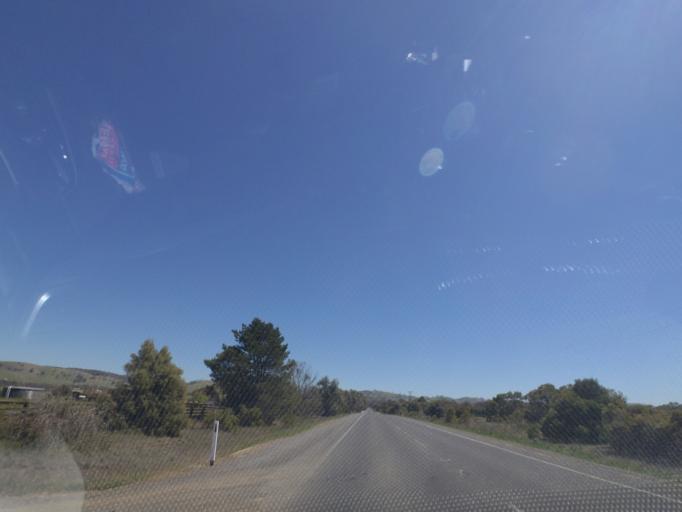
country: AU
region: Victoria
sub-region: Hume
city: Sunbury
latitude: -37.3064
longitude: 144.8376
